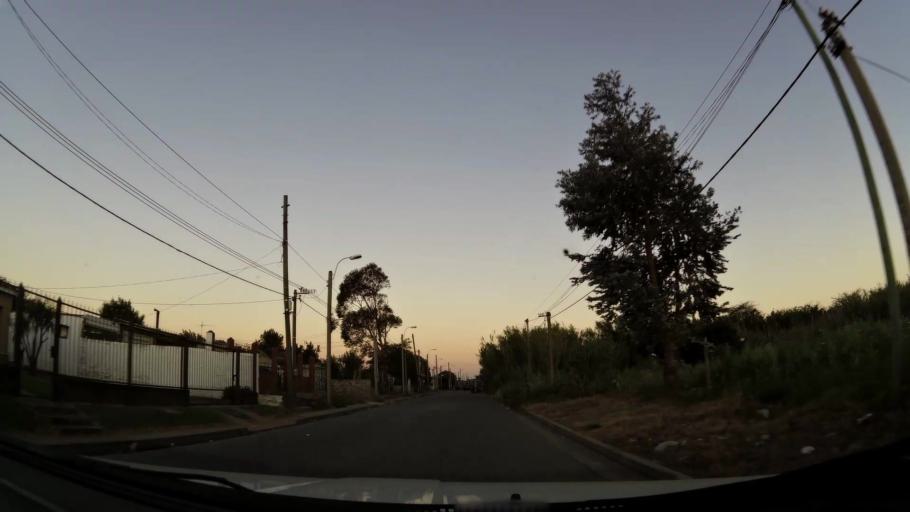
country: UY
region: Canelones
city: La Paz
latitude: -34.8183
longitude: -56.1524
